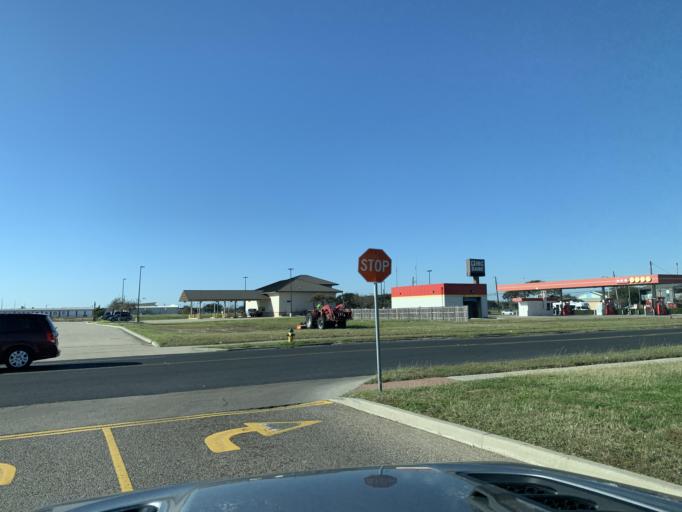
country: US
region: Texas
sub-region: Nueces County
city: Corpus Christi
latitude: 27.6653
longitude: -97.2831
